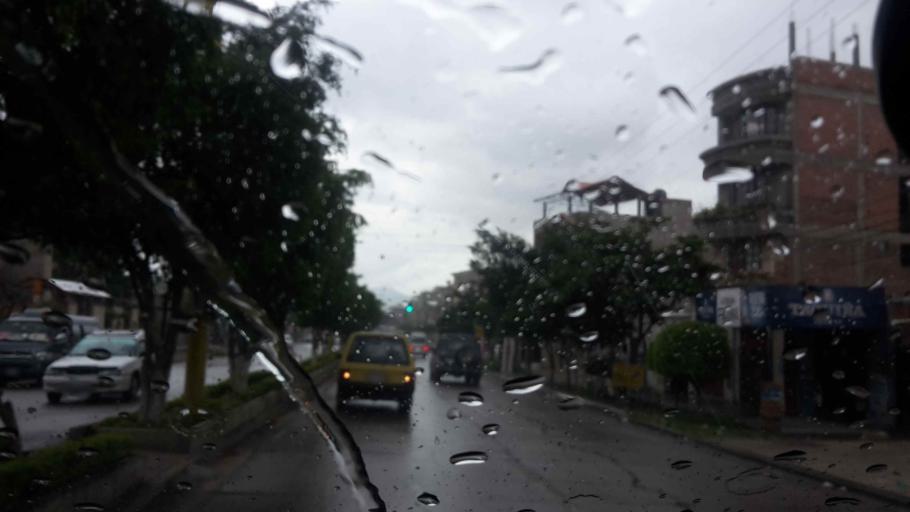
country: BO
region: Cochabamba
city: Cochabamba
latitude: -17.3514
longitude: -66.1907
